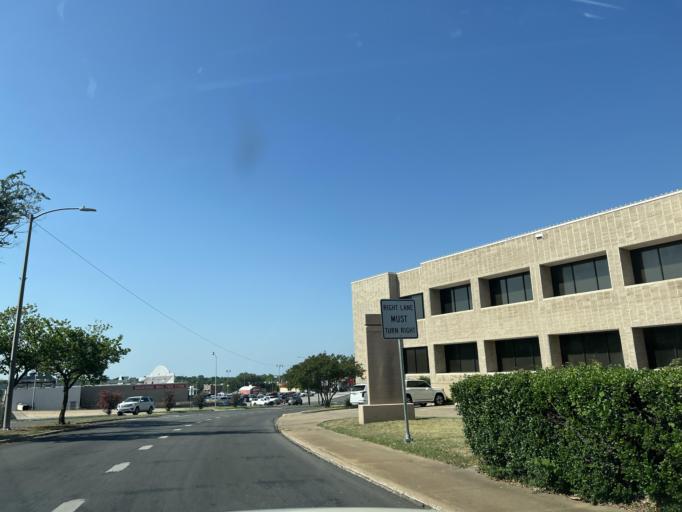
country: US
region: Texas
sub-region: Washington County
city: Brenham
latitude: 30.1676
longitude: -96.4001
